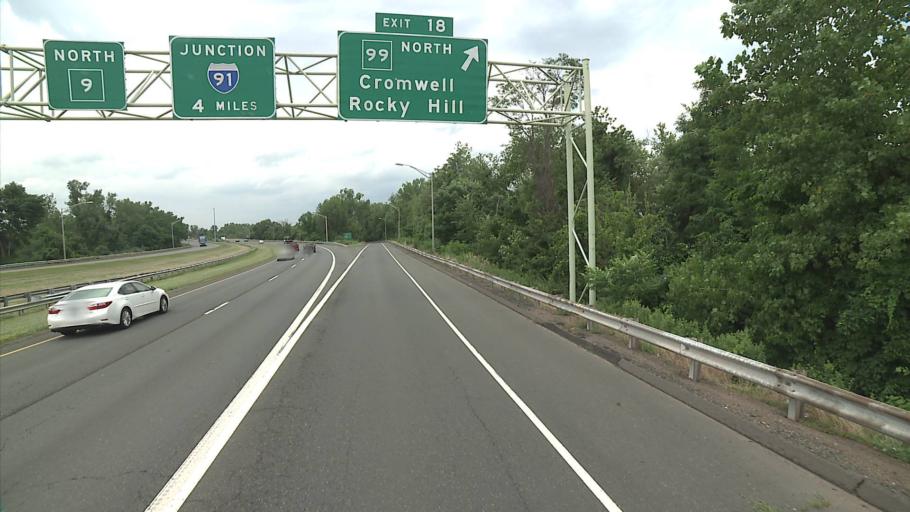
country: US
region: Connecticut
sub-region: Middlesex County
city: Portland
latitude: 41.5819
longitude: -72.6484
